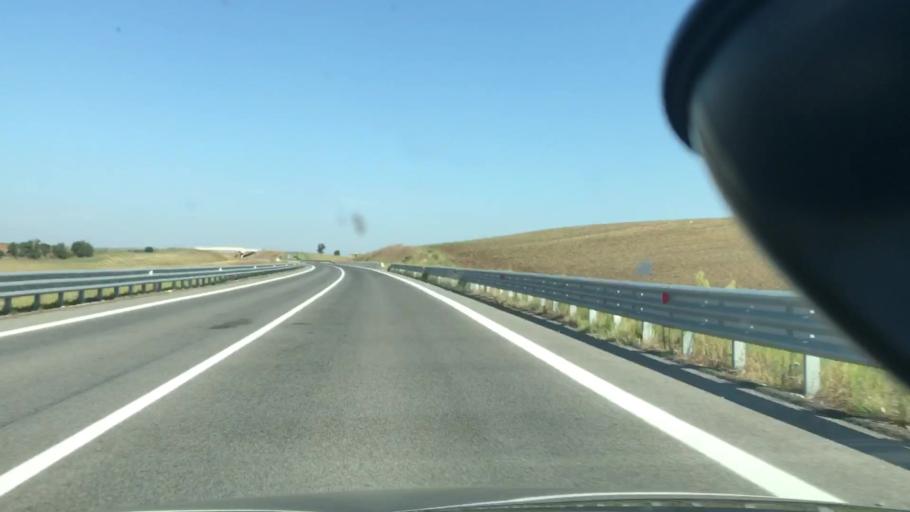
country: IT
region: Basilicate
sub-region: Provincia di Potenza
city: Palazzo San Gervasio
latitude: 40.9639
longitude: 16.0104
